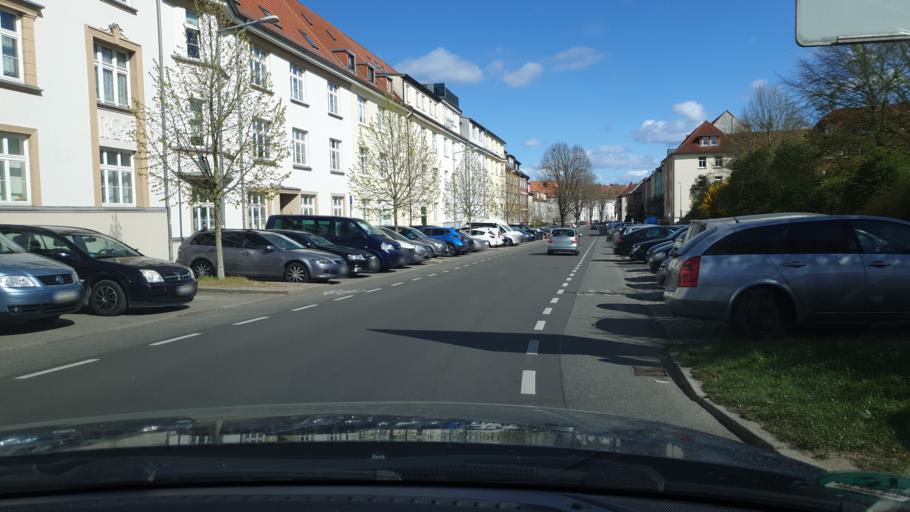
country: DE
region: Mecklenburg-Vorpommern
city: Weststadt
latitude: 53.6391
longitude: 11.3961
